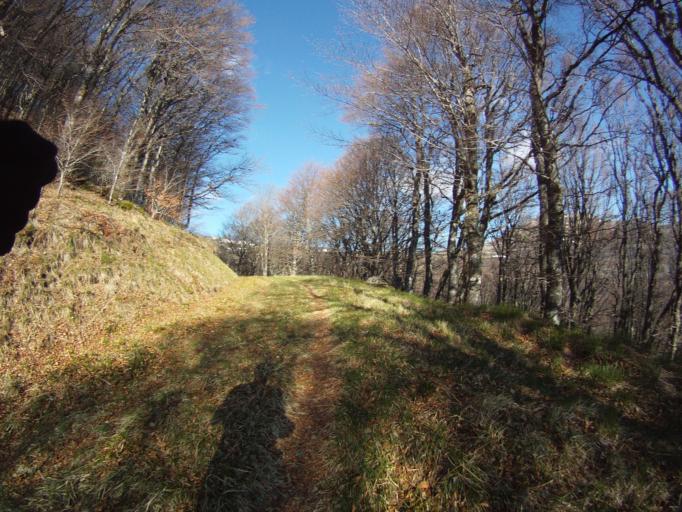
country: FR
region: Auvergne
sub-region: Departement du Puy-de-Dome
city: Mont-Dore
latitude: 45.5529
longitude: 2.8575
